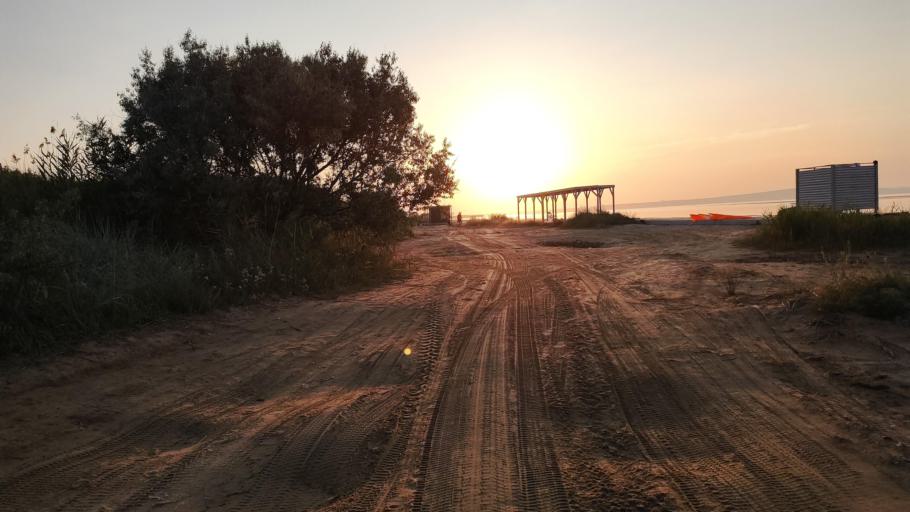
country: RU
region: Krasnodarskiy
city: Blagovetschenskaya
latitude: 45.0689
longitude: 37.0265
